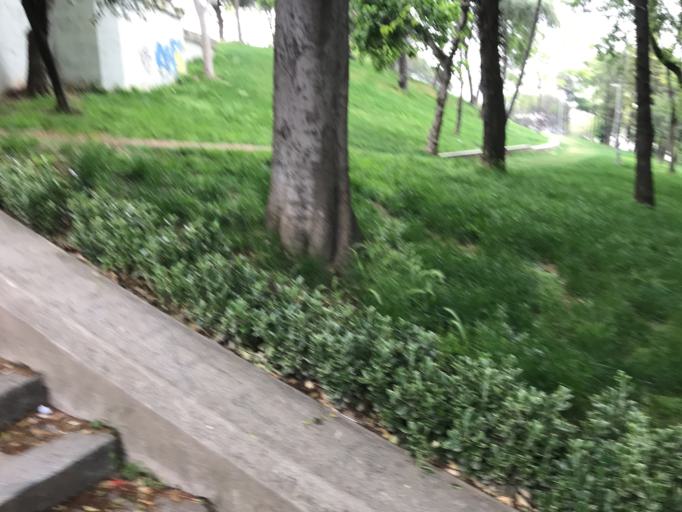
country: TR
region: Istanbul
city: Sisli
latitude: 41.0372
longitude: 28.9936
